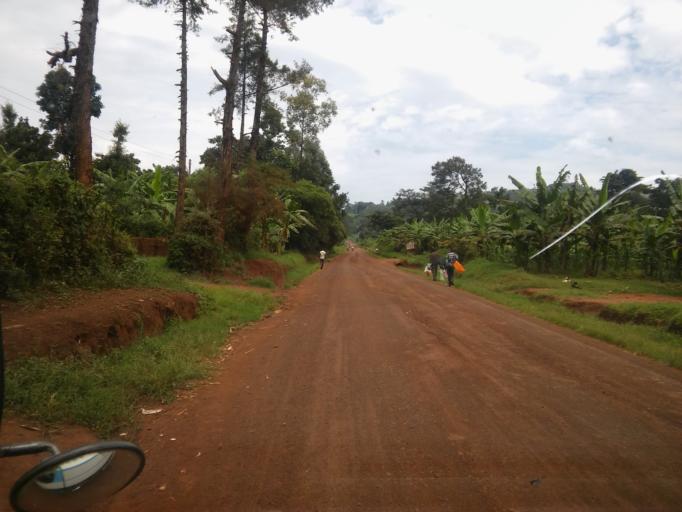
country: UG
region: Eastern Region
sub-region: Bududa District
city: Bududa
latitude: 0.9302
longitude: 34.2830
